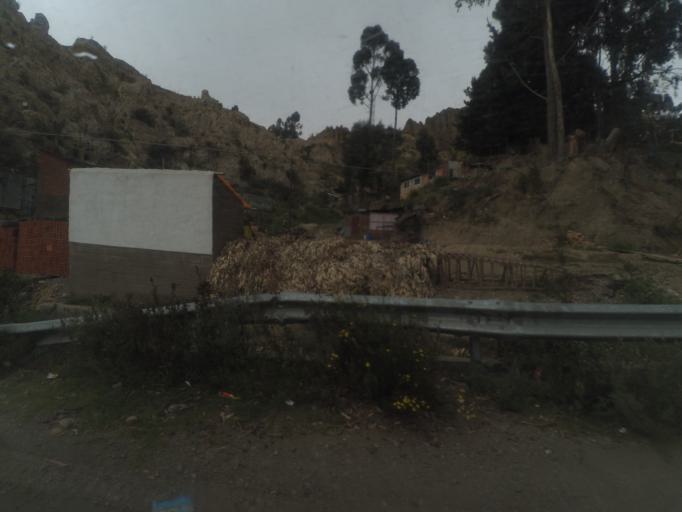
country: BO
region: La Paz
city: La Paz
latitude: -16.5638
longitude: -68.1749
